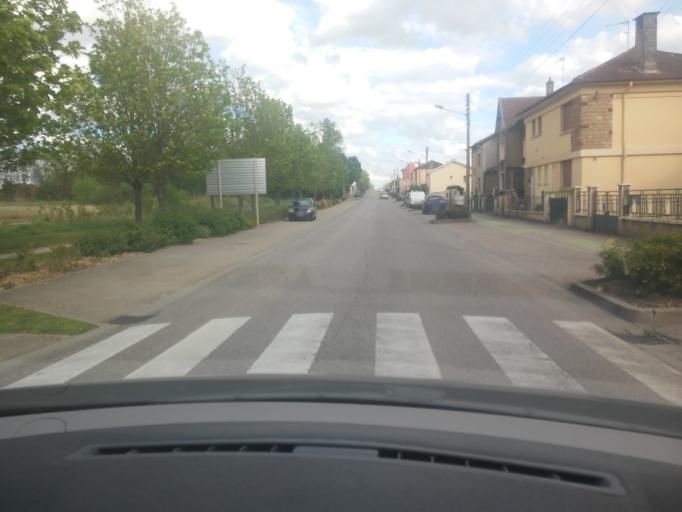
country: FR
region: Lorraine
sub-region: Departement de Meurthe-et-Moselle
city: Jarny
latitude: 49.1552
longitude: 5.8983
